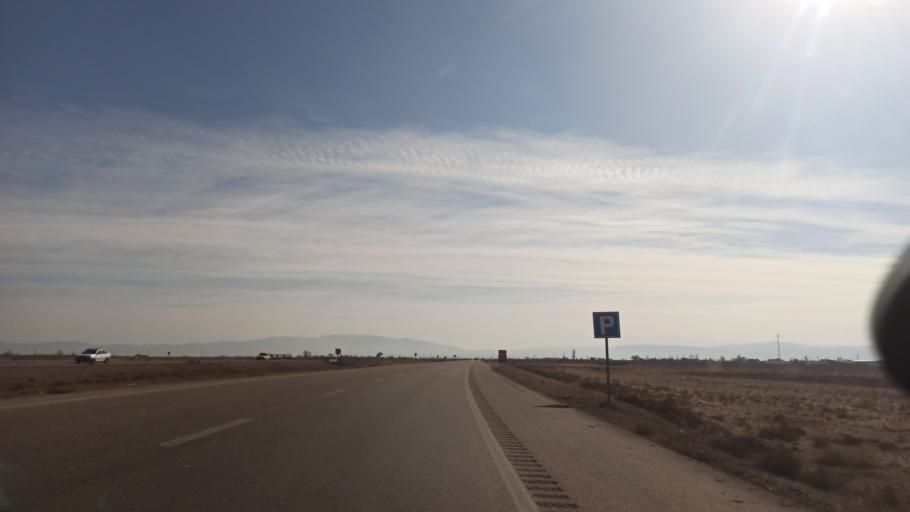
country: IR
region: Qazvin
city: Bu'in Zahra
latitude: 35.8311
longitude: 50.0741
